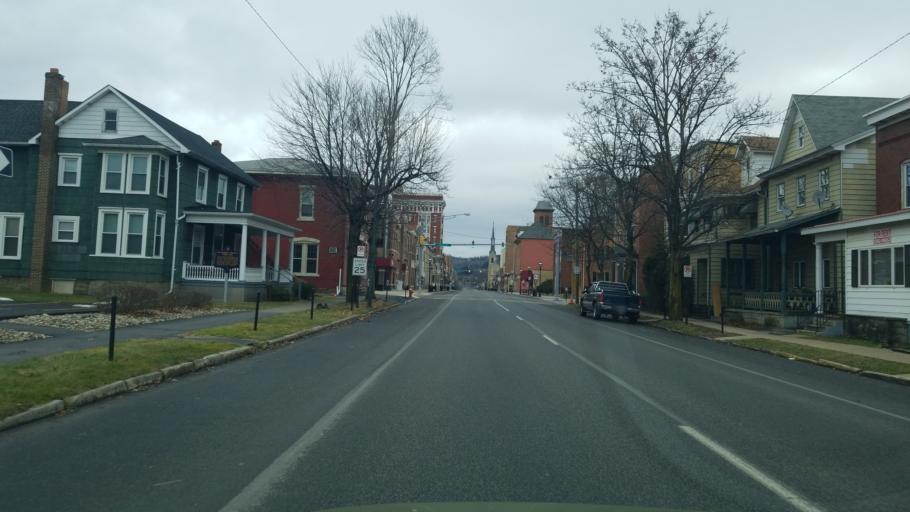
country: US
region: Pennsylvania
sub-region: Clearfield County
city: Clearfield
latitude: 41.0203
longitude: -78.4381
